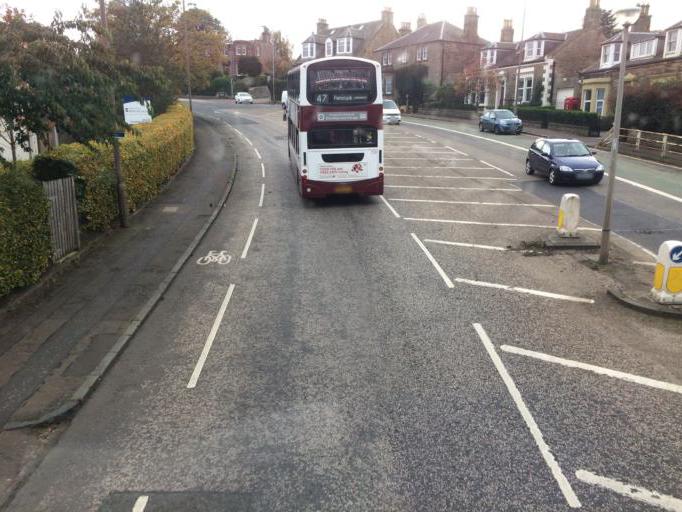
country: GB
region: Scotland
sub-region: Midlothian
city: Loanhead
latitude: 55.9170
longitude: -3.1677
